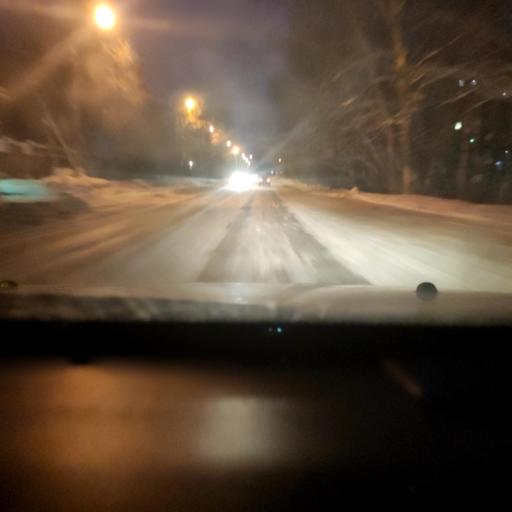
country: RU
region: Perm
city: Perm
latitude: 58.1172
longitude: 56.2876
